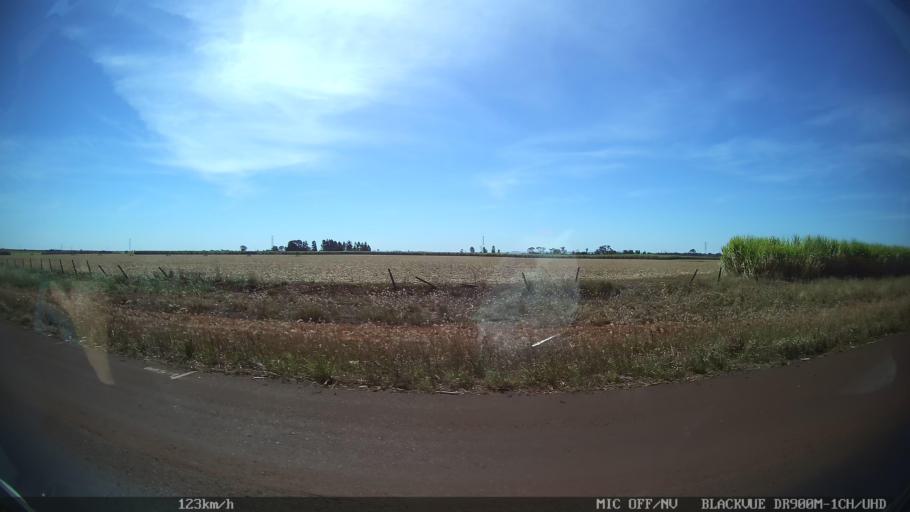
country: BR
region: Sao Paulo
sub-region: Ipua
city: Ipua
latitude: -20.5040
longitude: -47.9373
